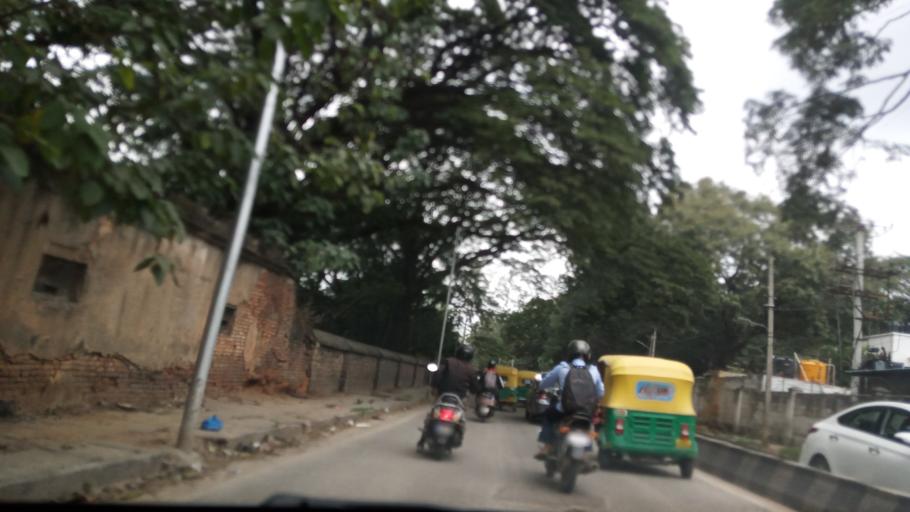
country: IN
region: Karnataka
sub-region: Bangalore Urban
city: Bangalore
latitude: 12.9965
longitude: 77.5958
